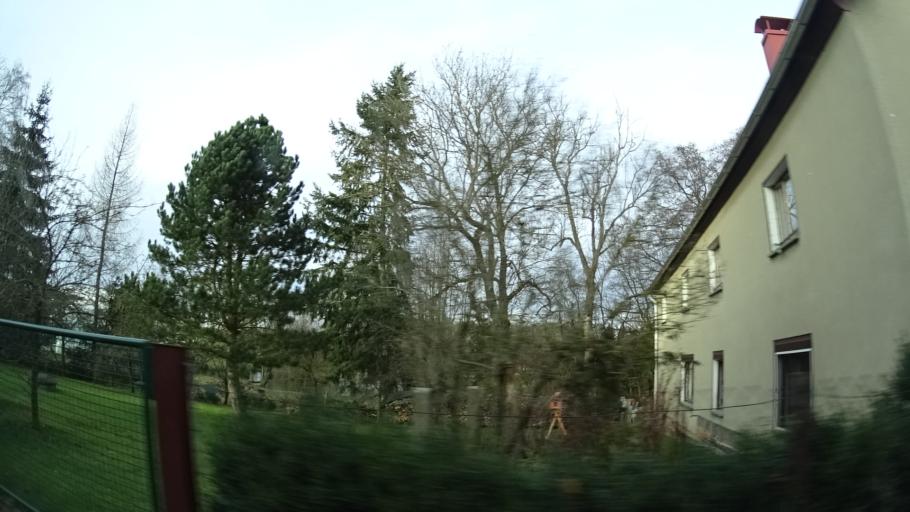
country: DE
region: Thuringia
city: Chursdorf
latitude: 50.6662
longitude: 11.8508
